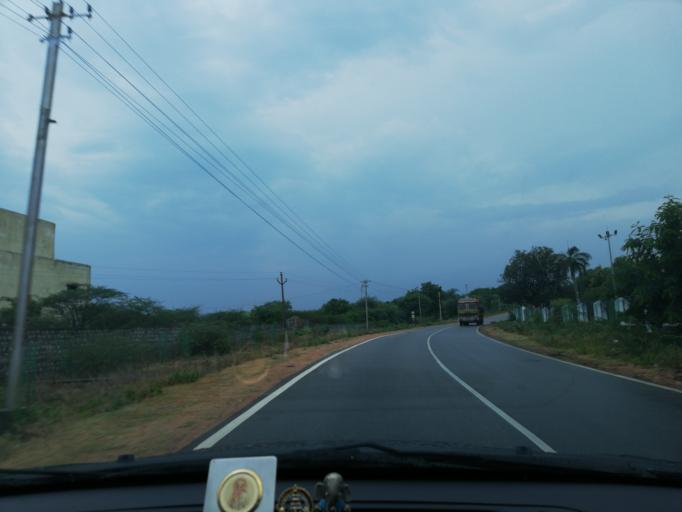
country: IN
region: Andhra Pradesh
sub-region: Guntur
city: Macherla
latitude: 16.6098
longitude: 79.2990
